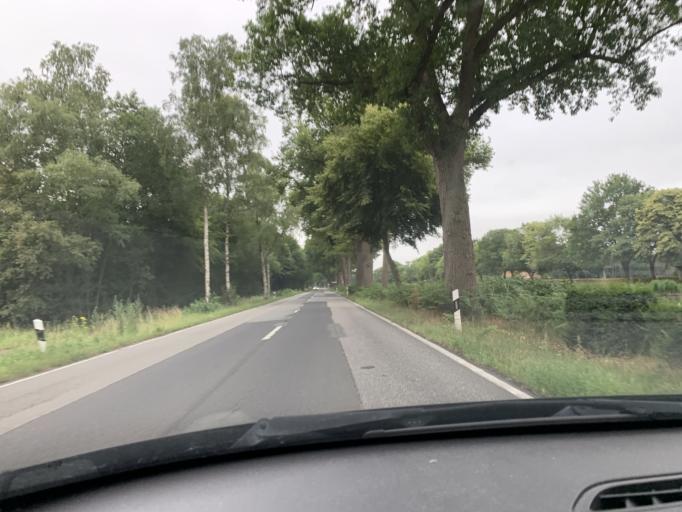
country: DE
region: Lower Saxony
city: Lingen
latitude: 52.4889
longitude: 7.2963
